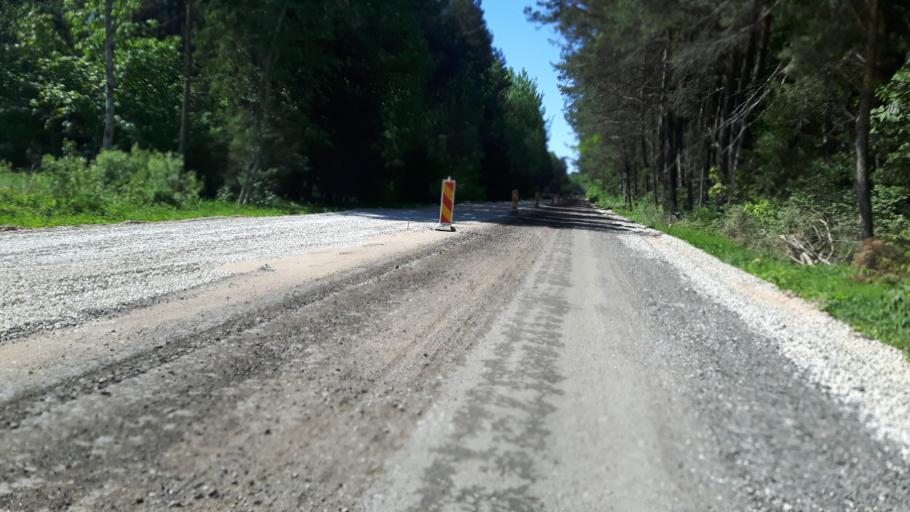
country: EE
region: Ida-Virumaa
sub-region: Narva-Joesuu linn
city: Narva-Joesuu
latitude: 59.4224
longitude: 27.9797
